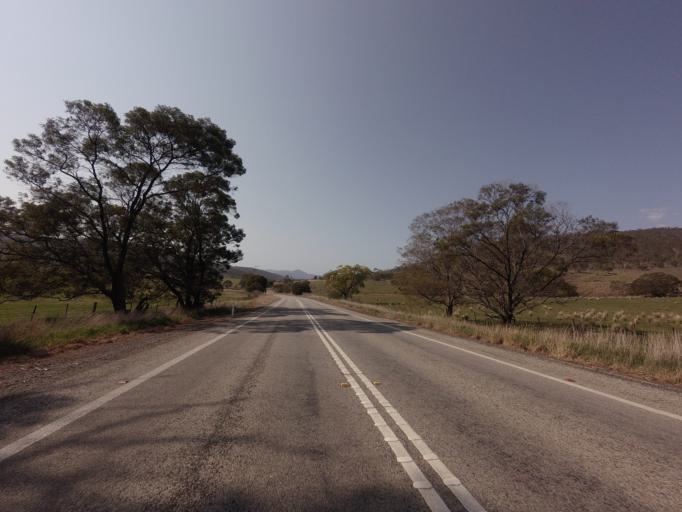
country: AU
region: Tasmania
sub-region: Northern Midlands
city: Evandale
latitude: -41.8183
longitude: 147.5458
